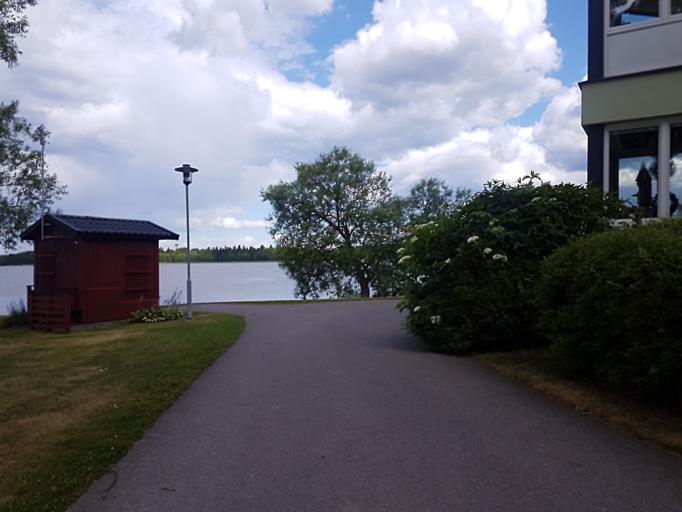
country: SE
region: Soedermanland
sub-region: Gnesta Kommun
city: Gnesta
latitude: 59.0488
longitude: 17.3169
